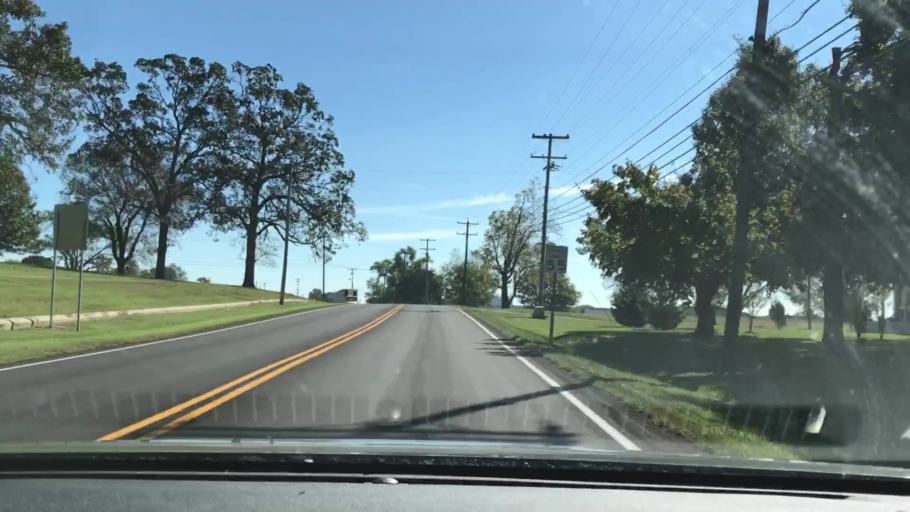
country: US
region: Kentucky
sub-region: Christian County
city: Hopkinsville
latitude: 36.8630
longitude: -87.4509
